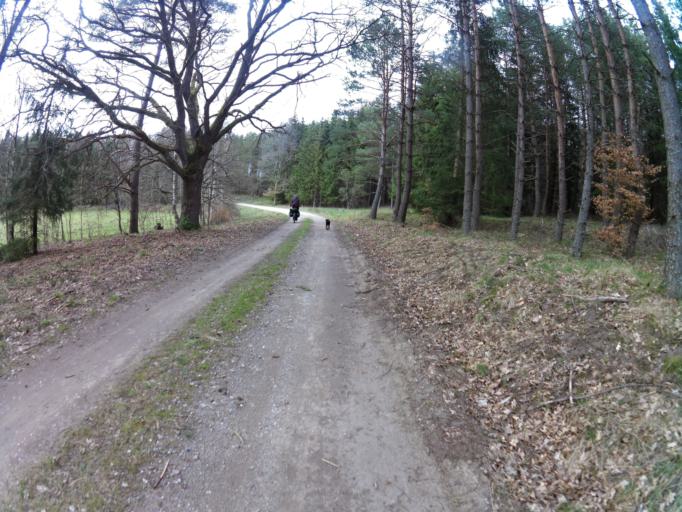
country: PL
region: West Pomeranian Voivodeship
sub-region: Powiat szczecinecki
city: Bialy Bor
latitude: 53.8843
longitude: 16.7202
